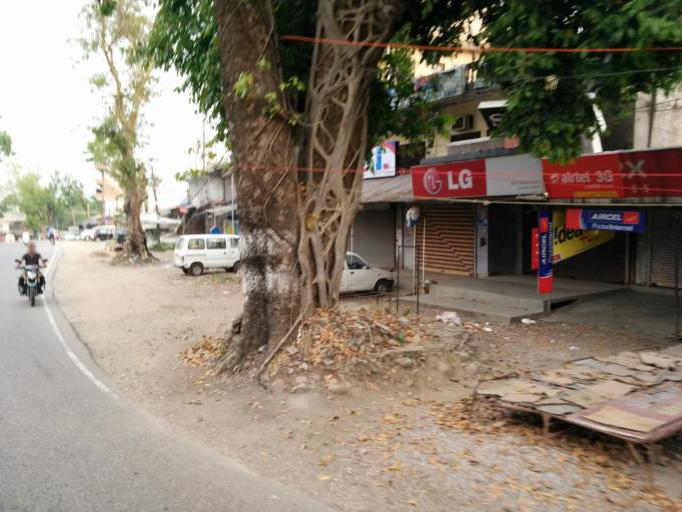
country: IN
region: Himachal Pradesh
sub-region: Kangra
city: Yol
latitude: 32.1857
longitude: 76.2122
